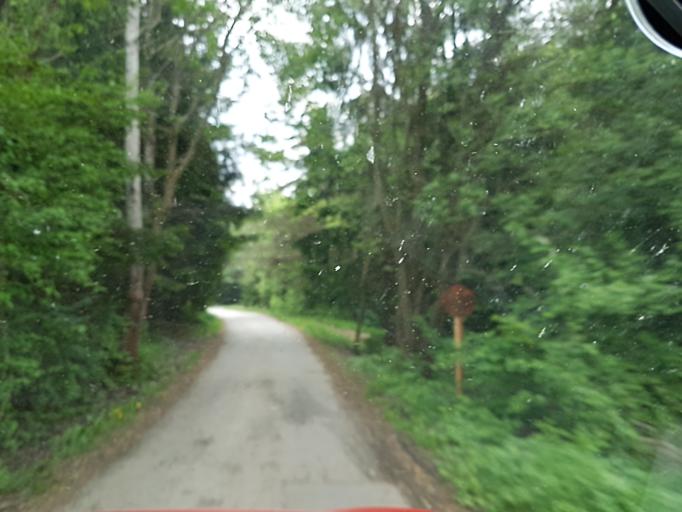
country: SK
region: Zilinsky
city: Ruzomberok
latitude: 49.0726
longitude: 19.2817
